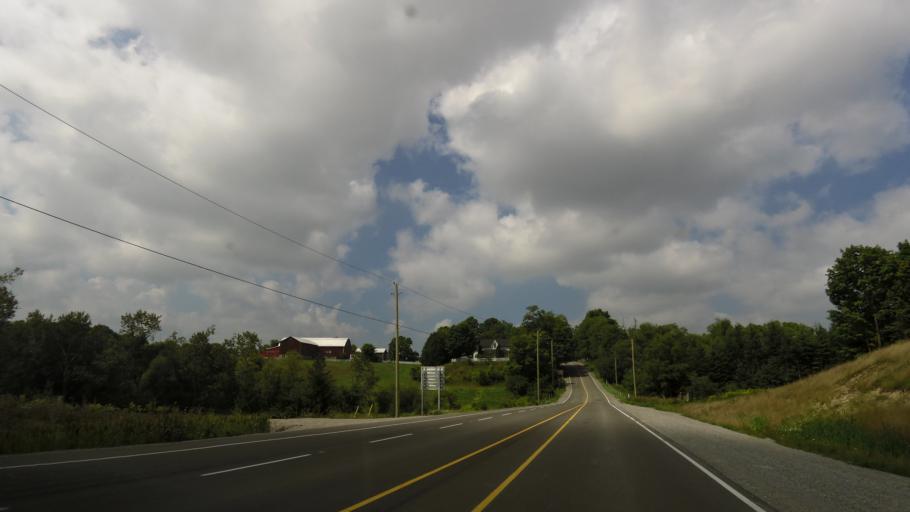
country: CA
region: Ontario
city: Oshawa
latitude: 43.9852
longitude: -78.8695
